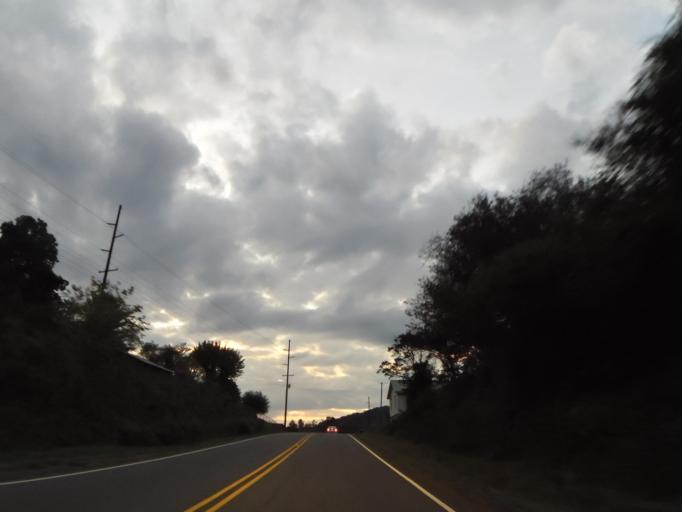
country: US
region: North Carolina
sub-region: Madison County
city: Marshall
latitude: 35.8159
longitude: -82.6984
